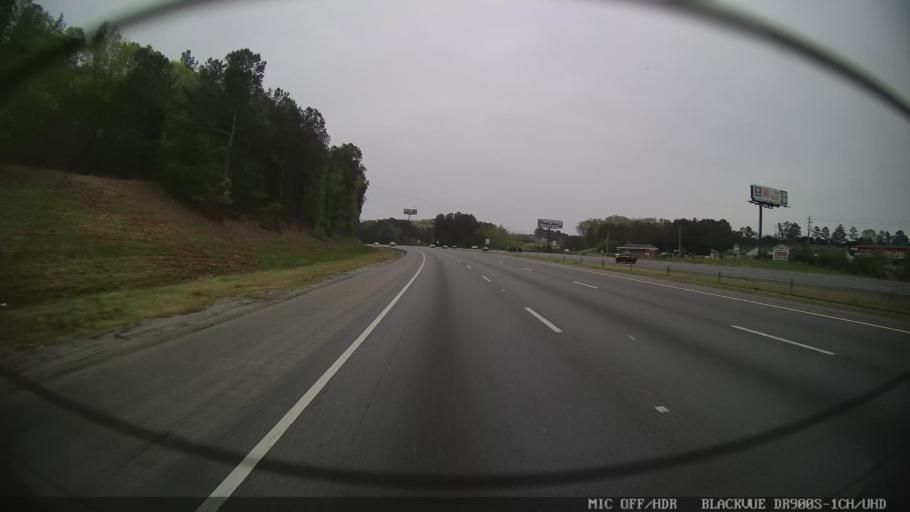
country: US
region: Georgia
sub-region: Bartow County
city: Cartersville
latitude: 34.2153
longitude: -84.7553
